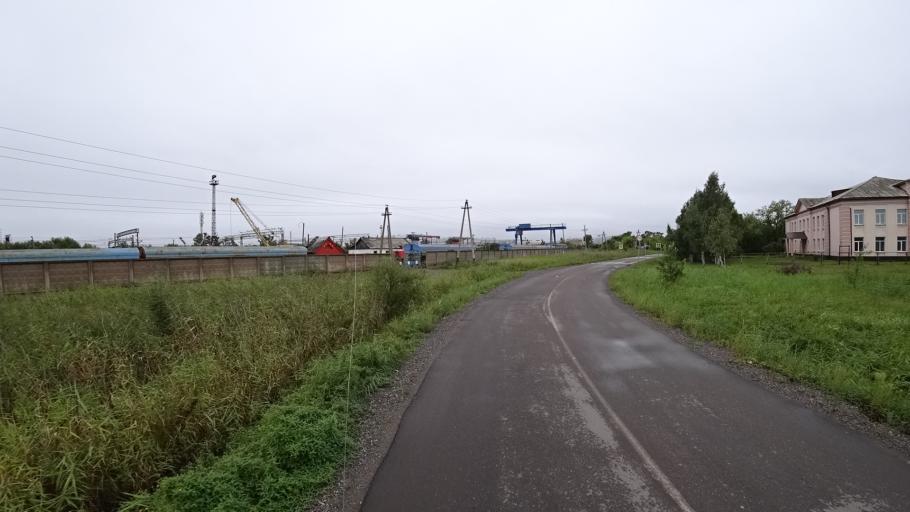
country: RU
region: Primorskiy
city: Monastyrishche
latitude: 44.2099
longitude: 132.4380
